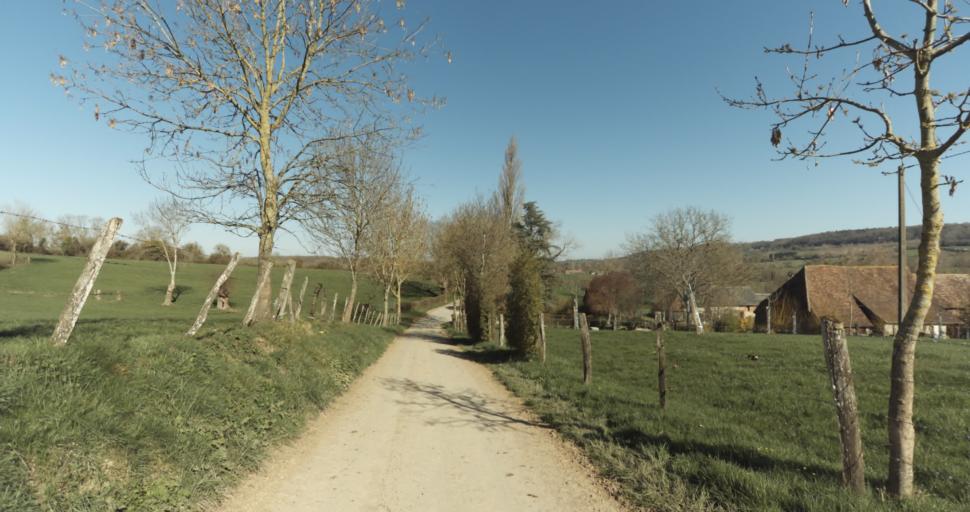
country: FR
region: Lower Normandy
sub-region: Departement du Calvados
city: Saint-Pierre-sur-Dives
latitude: 48.9679
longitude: 0.0389
